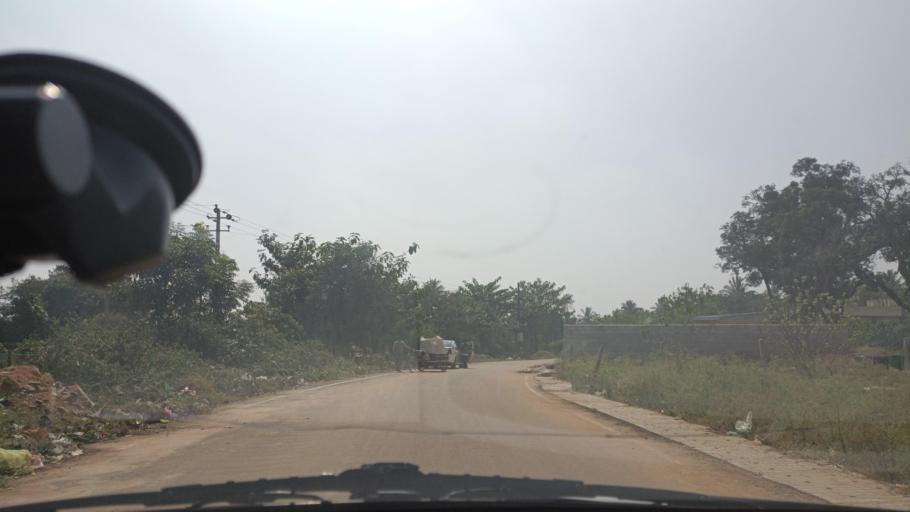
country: IN
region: Karnataka
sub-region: Bangalore Urban
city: Yelahanka
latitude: 13.1151
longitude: 77.6153
